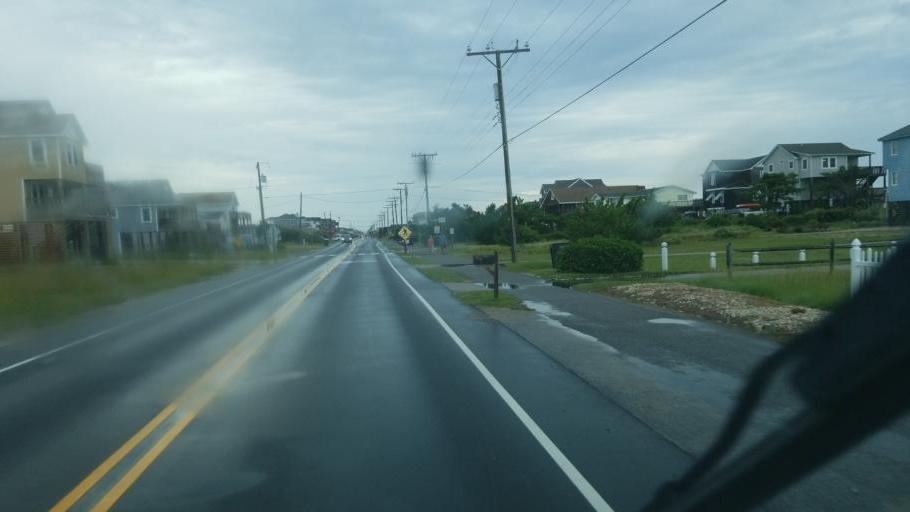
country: US
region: North Carolina
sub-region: Dare County
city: Nags Head
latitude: 35.9802
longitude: -75.6371
